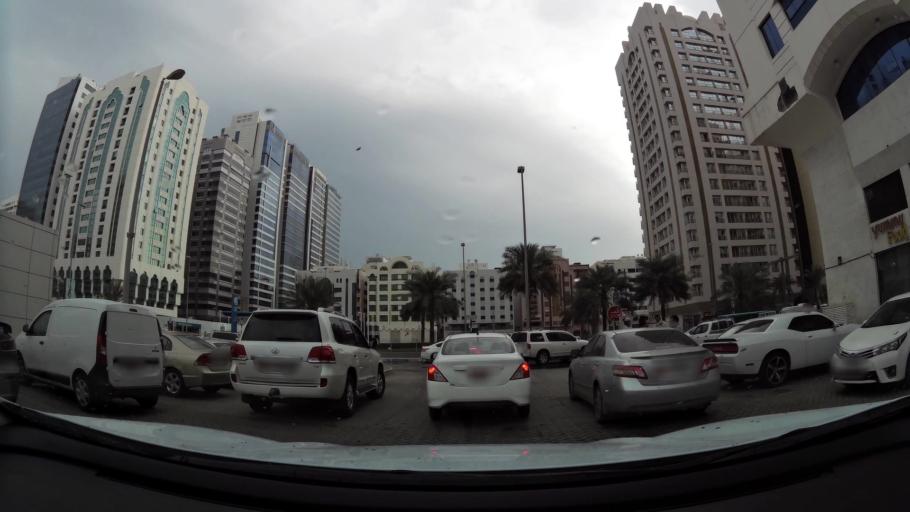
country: AE
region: Abu Dhabi
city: Abu Dhabi
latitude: 24.4886
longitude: 54.3707
